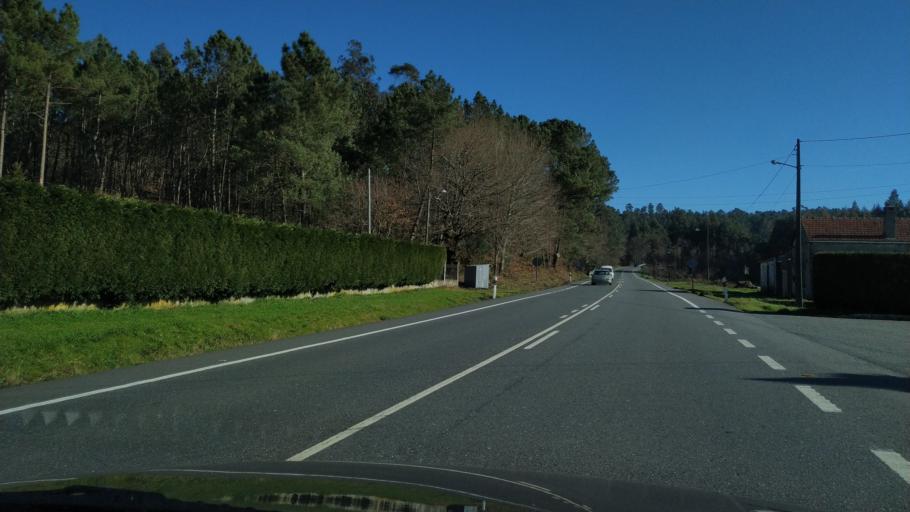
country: ES
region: Galicia
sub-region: Provincia da Coruna
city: Ribeira
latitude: 42.7533
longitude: -8.3825
